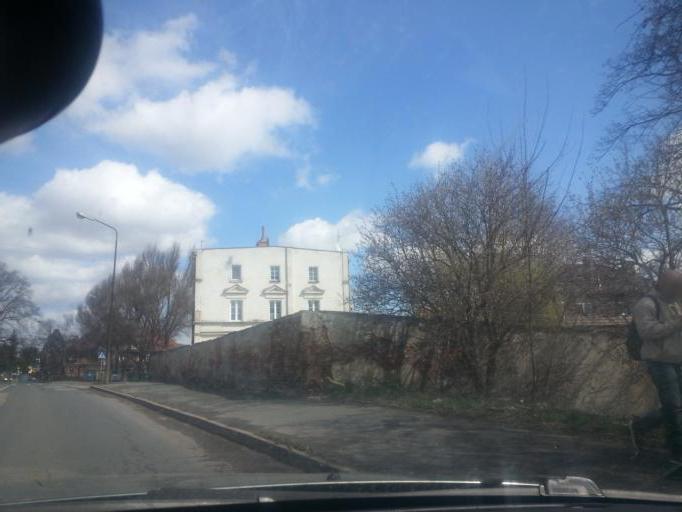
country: PL
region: Lower Silesian Voivodeship
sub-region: Jelenia Gora
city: Jelenia Gora
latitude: 50.8999
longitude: 15.7196
